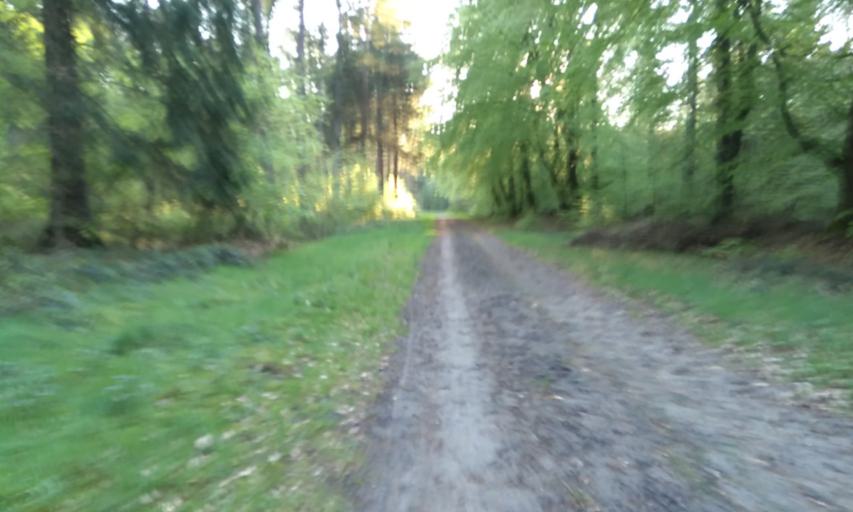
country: DE
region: Lower Saxony
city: Dollern
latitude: 53.5142
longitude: 9.5169
